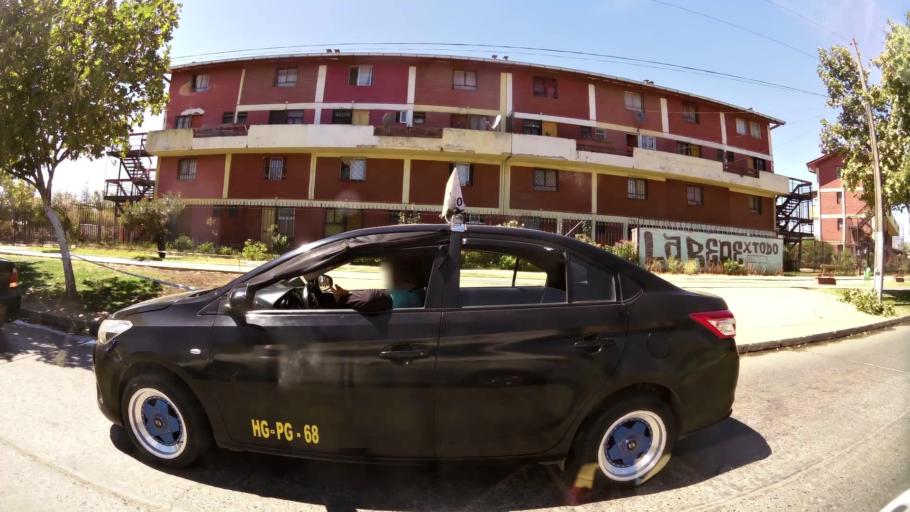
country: CL
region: O'Higgins
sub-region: Provincia de Cachapoal
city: Rancagua
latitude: -34.1591
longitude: -70.7202
